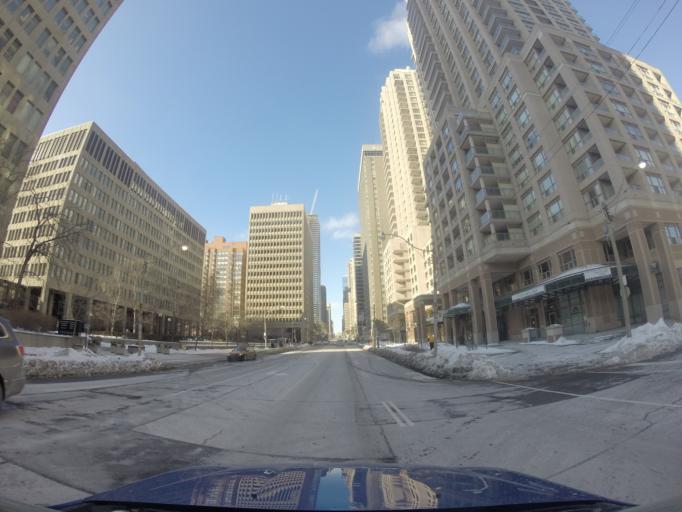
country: CA
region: Ontario
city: Toronto
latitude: 43.6633
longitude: -79.3867
